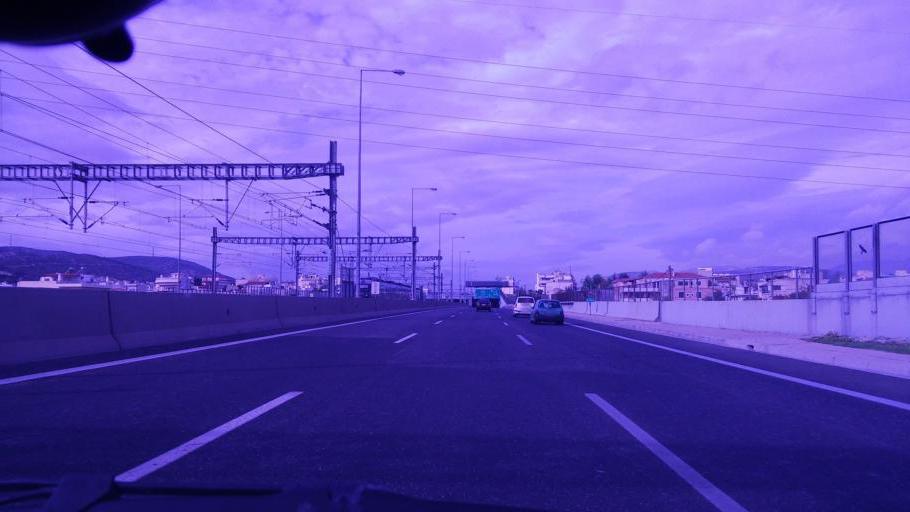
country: GR
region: Attica
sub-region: Nomarchia Dytikis Attikis
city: Zefyri
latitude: 38.0688
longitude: 23.7240
